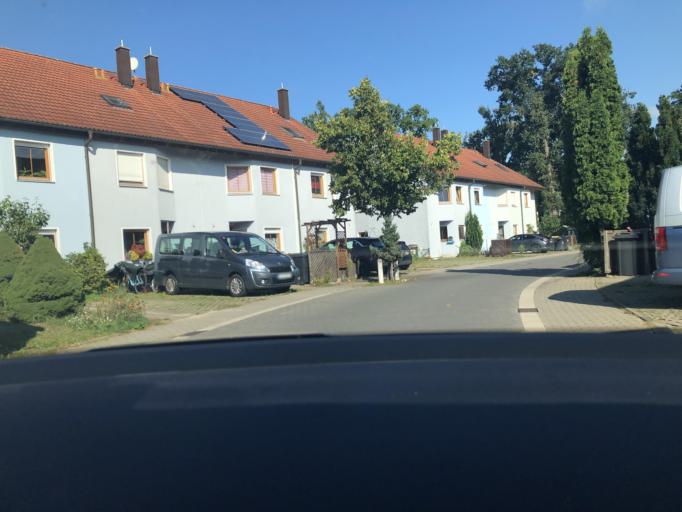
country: DE
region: Brandenburg
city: Erkner
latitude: 52.4075
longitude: 13.7479
